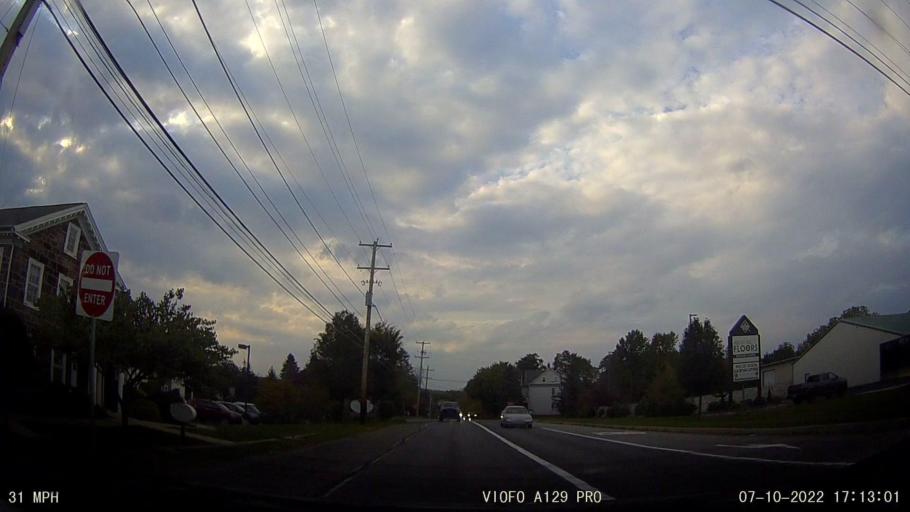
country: US
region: Pennsylvania
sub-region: Berks County
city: Amity Gardens
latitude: 40.2596
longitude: -75.7311
